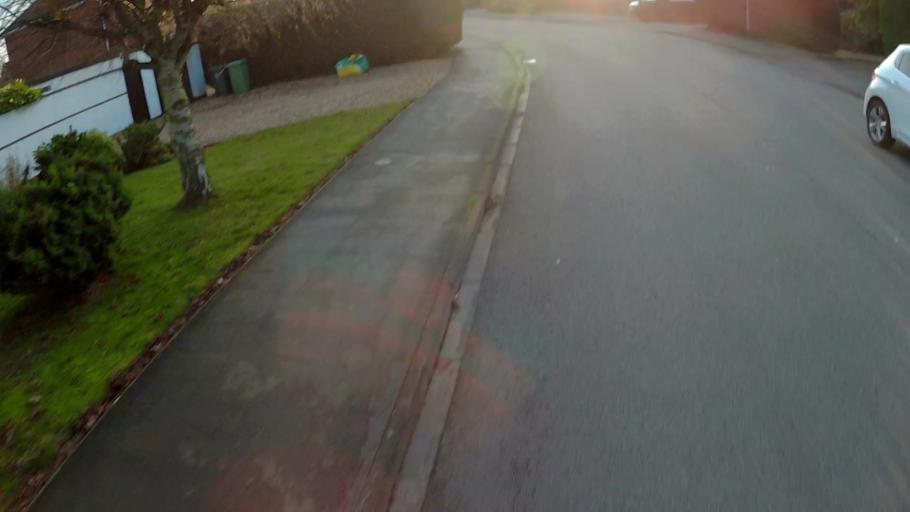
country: GB
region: England
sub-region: Lincolnshire
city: Bourne
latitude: 52.7701
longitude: -0.3927
